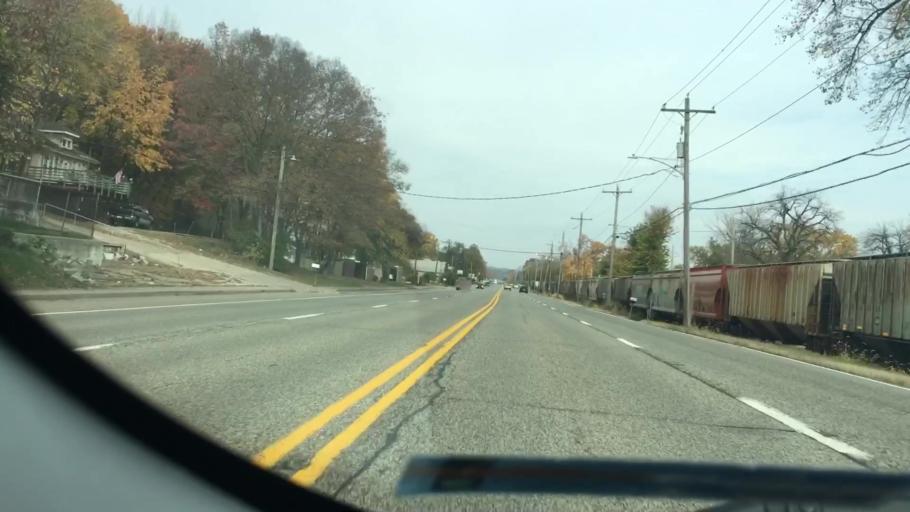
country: US
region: Illinois
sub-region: Peoria County
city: Peoria Heights
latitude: 40.7438
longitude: -89.5554
